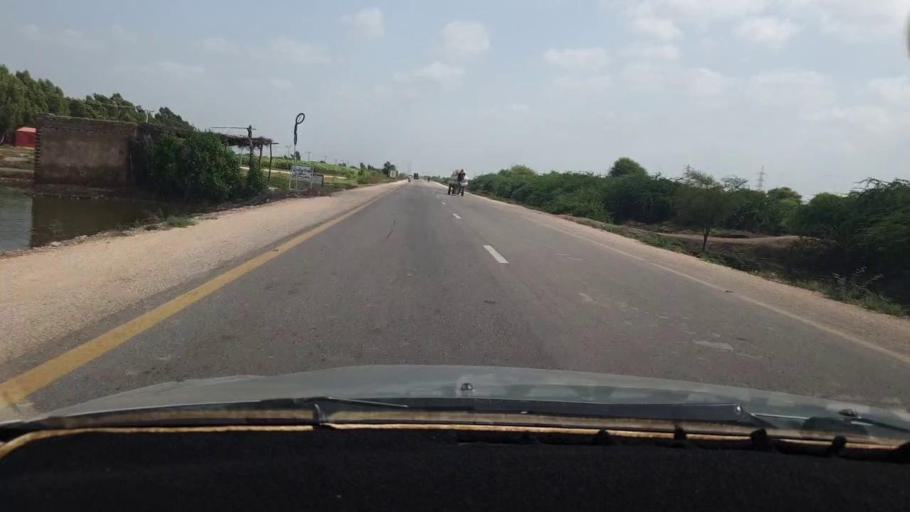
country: PK
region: Sindh
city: Digri
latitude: 25.0417
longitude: 69.2335
